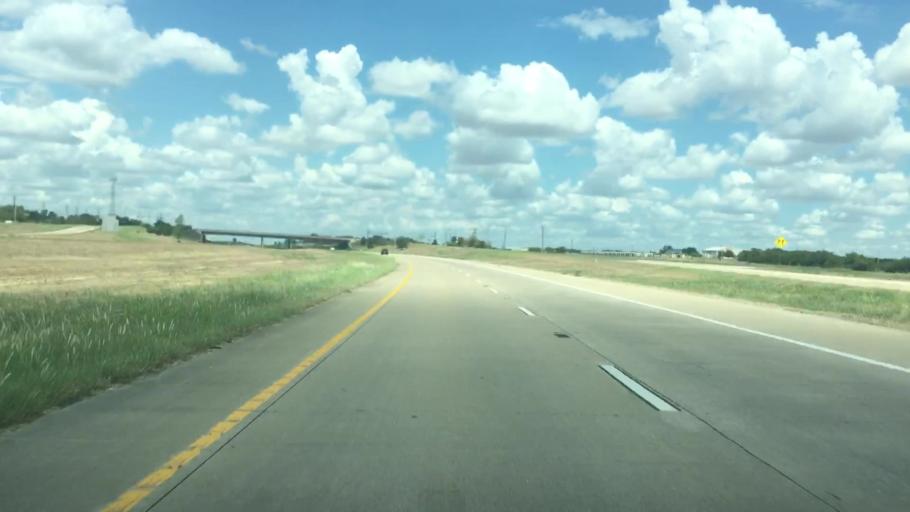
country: US
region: Texas
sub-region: Williamson County
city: Georgetown
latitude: 30.6371
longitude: -97.6283
